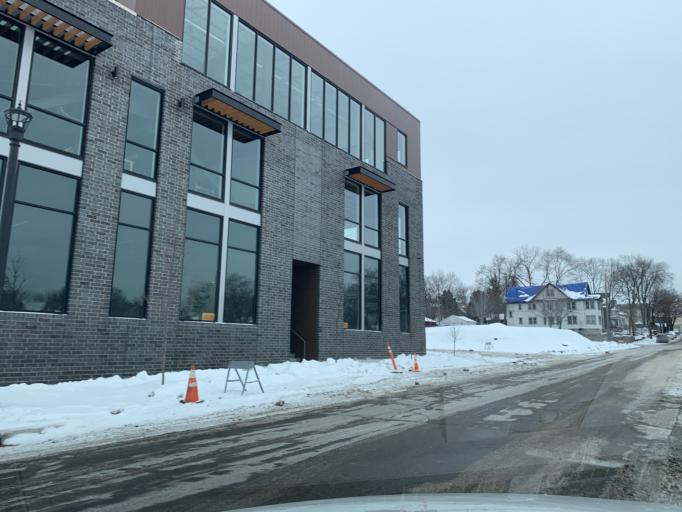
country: US
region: Minnesota
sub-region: Hennepin County
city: Minneapolis
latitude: 44.9781
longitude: -93.2994
